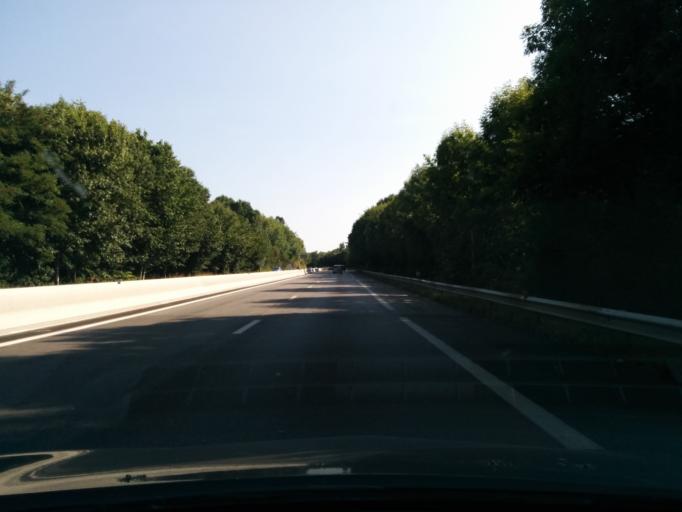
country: FR
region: Limousin
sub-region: Departement de la Haute-Vienne
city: Condat-sur-Vienne
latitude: 45.8045
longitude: 1.2971
